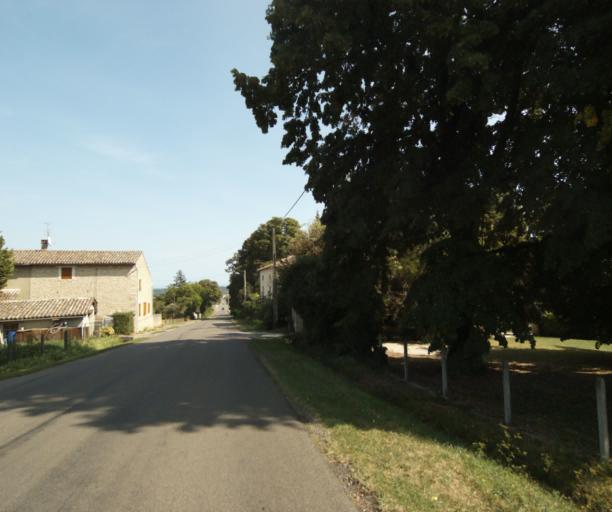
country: FR
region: Bourgogne
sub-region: Departement de Saone-et-Loire
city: Tournus
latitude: 46.5687
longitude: 4.8911
